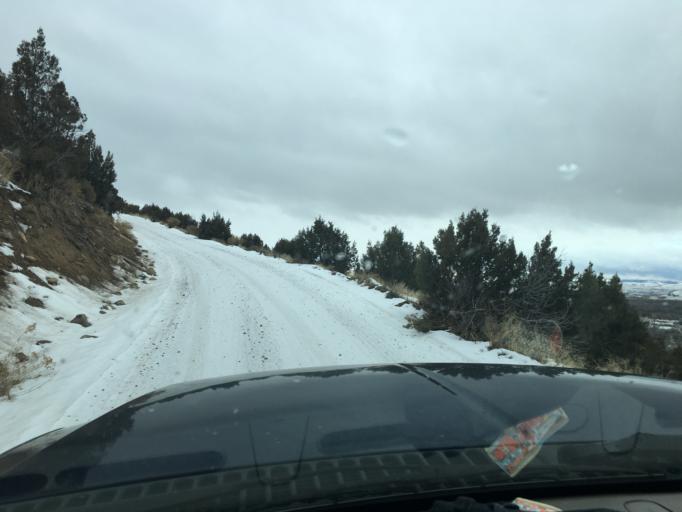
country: US
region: Colorado
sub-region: Garfield County
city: Parachute
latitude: 39.3493
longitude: -108.1731
